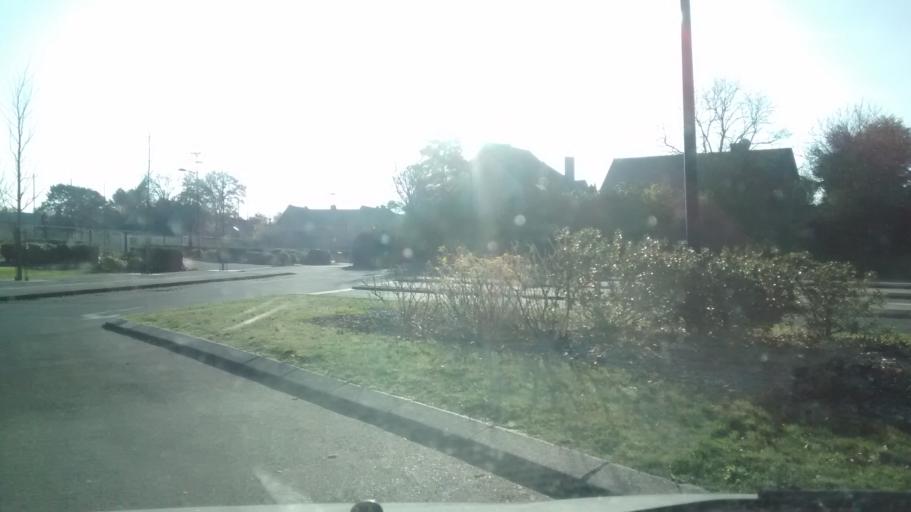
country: FR
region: Brittany
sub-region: Departement d'Ille-et-Vilaine
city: Pace
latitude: 48.1525
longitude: -1.7713
